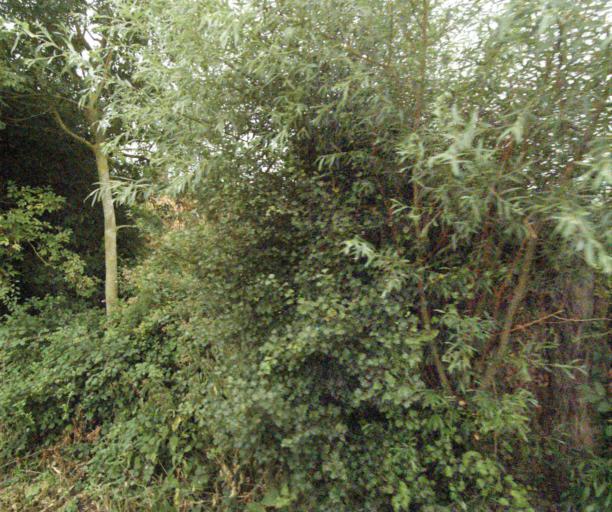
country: FR
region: Nord-Pas-de-Calais
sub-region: Departement du Nord
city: Bondues
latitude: 50.7175
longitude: 3.0937
